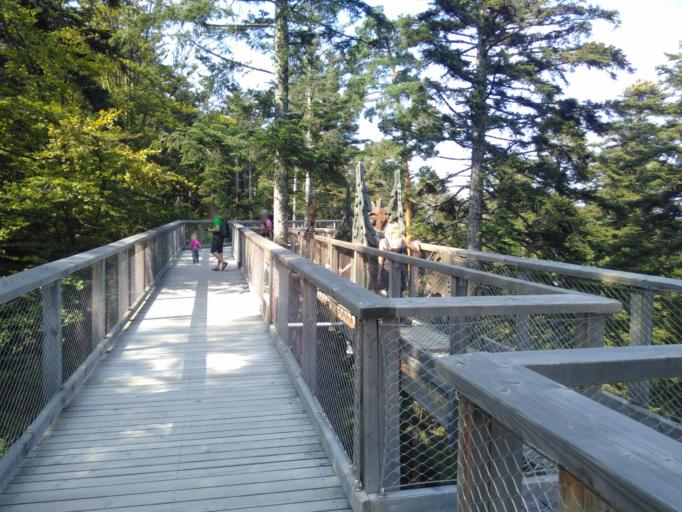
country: DE
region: Baden-Wuerttemberg
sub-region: Karlsruhe Region
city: Bad Wildbad
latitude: 48.7506
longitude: 8.5345
